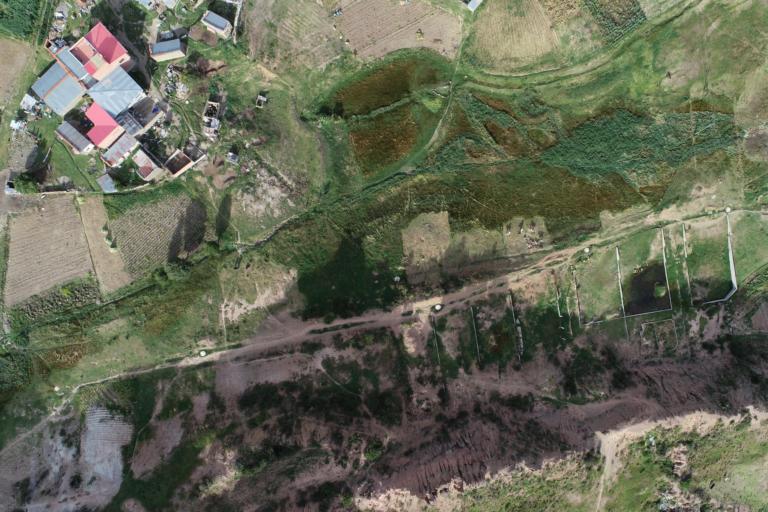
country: BO
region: La Paz
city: La Paz
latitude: -16.5465
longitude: -68.0021
